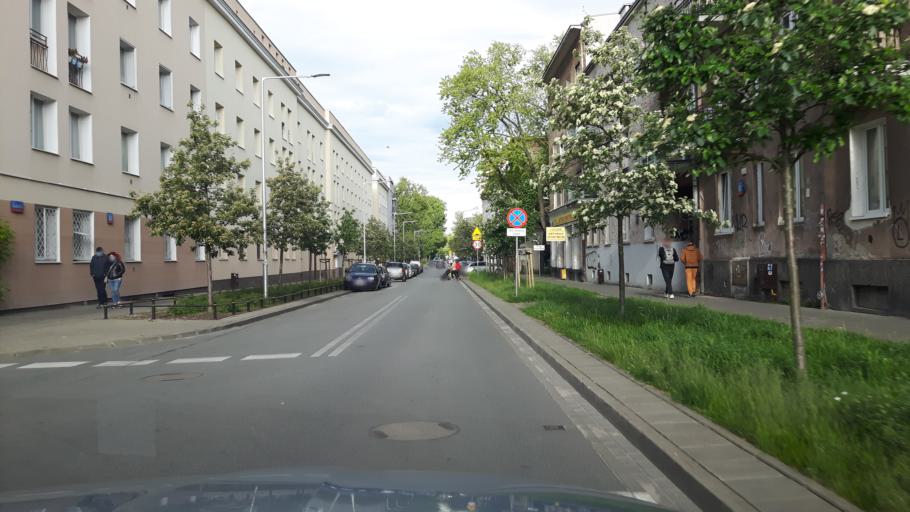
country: PL
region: Masovian Voivodeship
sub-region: Warszawa
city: Praga Poludnie
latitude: 52.2474
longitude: 21.0818
